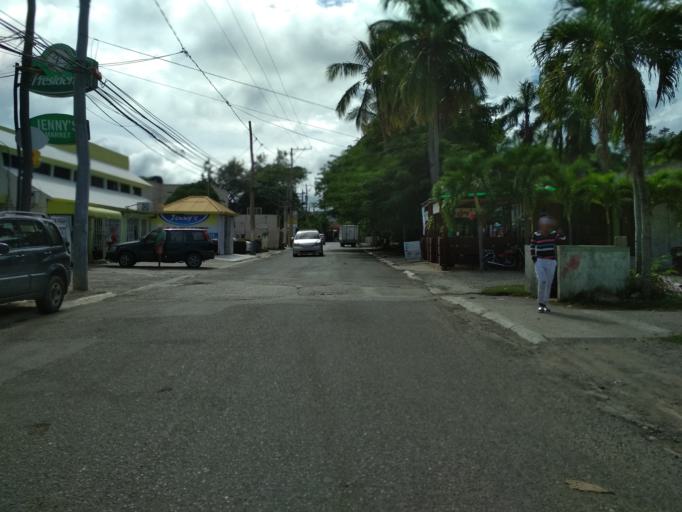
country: DO
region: Puerto Plata
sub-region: Puerto Plata
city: Puerto Plata
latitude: 19.8082
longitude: -70.7135
